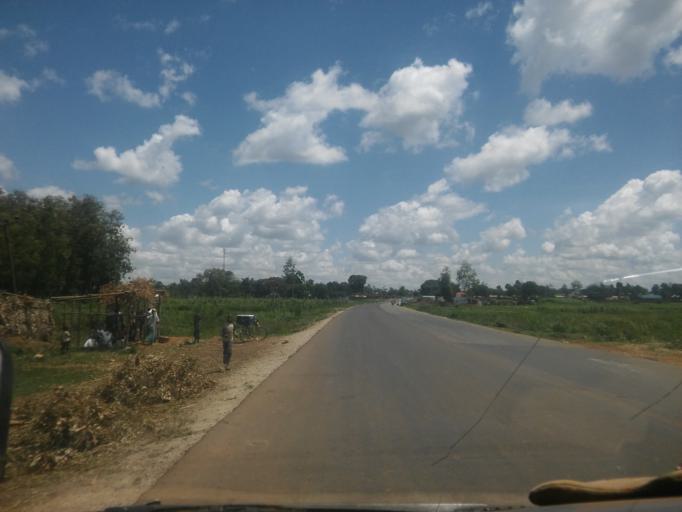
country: UG
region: Eastern Region
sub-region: Mbale District
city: Mbale
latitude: 1.0743
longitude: 34.1241
